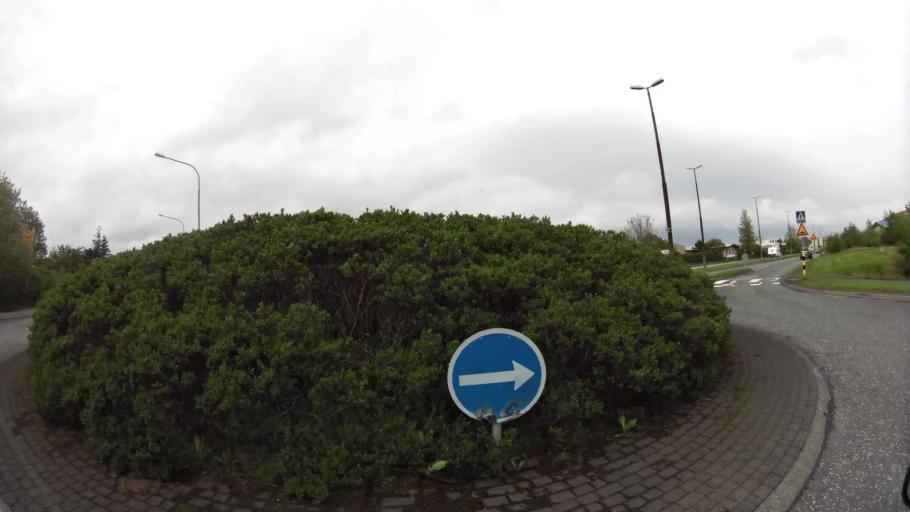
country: IS
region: Capital Region
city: Hafnarfjoerdur
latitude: 64.0775
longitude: -21.9659
